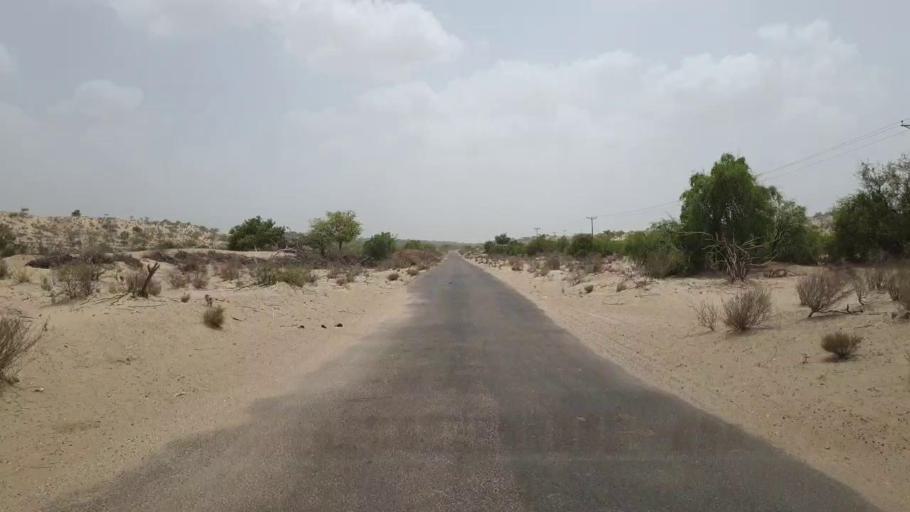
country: PK
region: Sindh
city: Diplo
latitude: 24.3982
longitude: 69.4655
